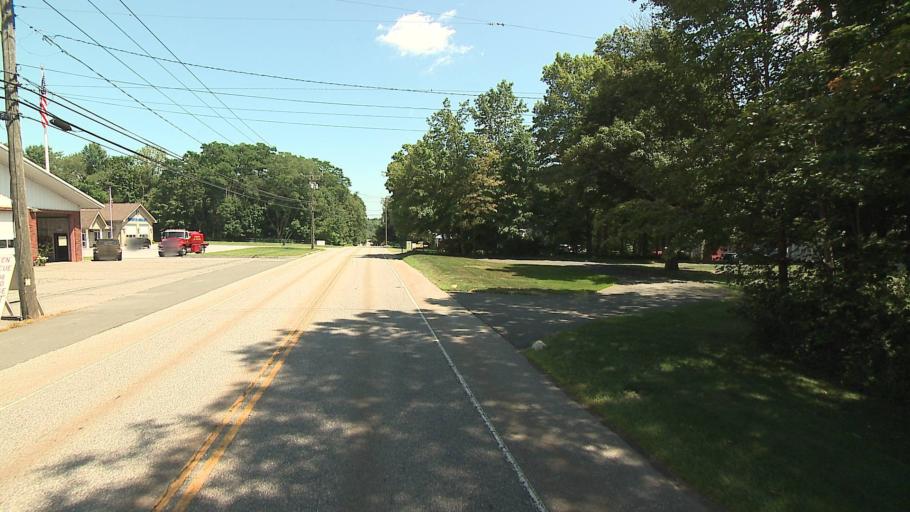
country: US
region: Connecticut
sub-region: Litchfield County
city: Northwest Harwinton
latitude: 41.7735
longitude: -73.0464
